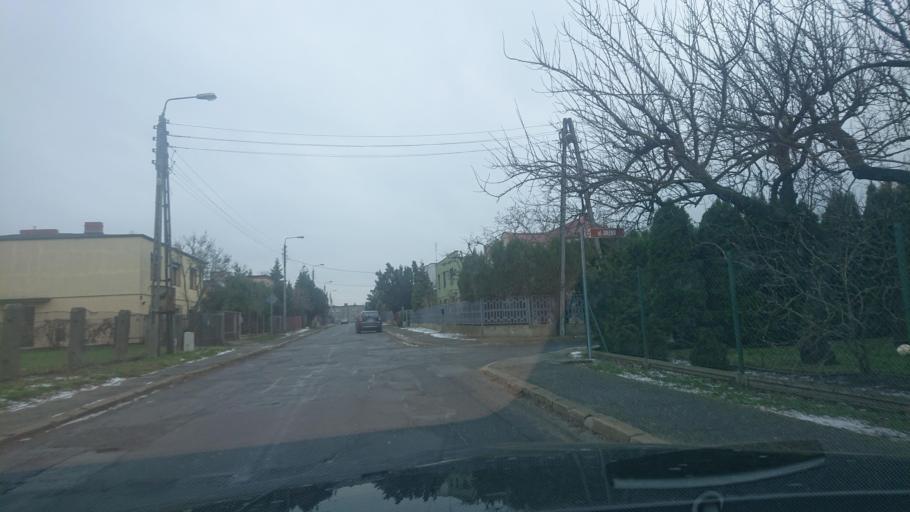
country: PL
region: Greater Poland Voivodeship
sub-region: Powiat gnieznienski
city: Gniezno
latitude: 52.5410
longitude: 17.5765
